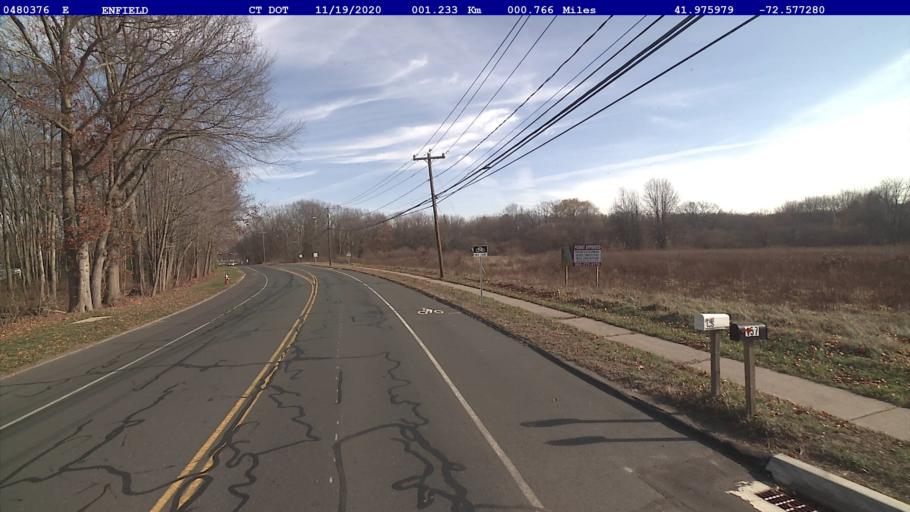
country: US
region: Connecticut
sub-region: Hartford County
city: Enfield
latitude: 41.9761
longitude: -72.5774
